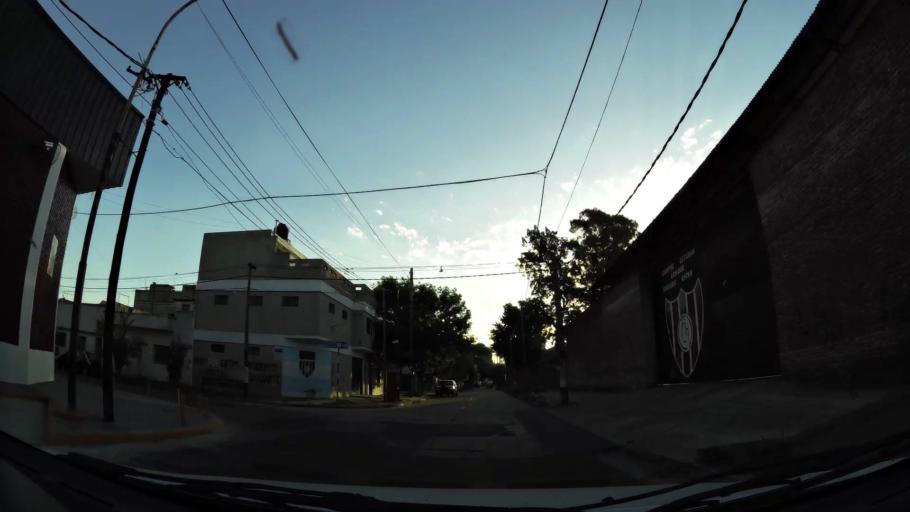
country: AR
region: Buenos Aires
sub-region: Partido de General San Martin
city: General San Martin
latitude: -34.5650
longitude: -58.5233
